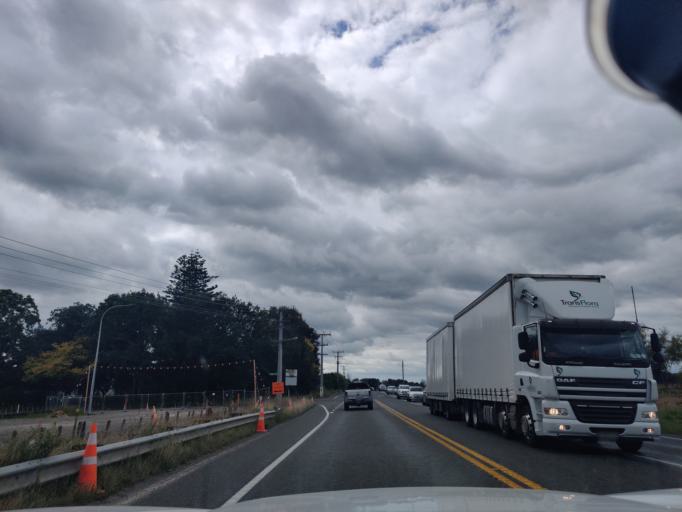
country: NZ
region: Wellington
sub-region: Kapiti Coast District
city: Otaki
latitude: -40.7475
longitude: 175.1673
